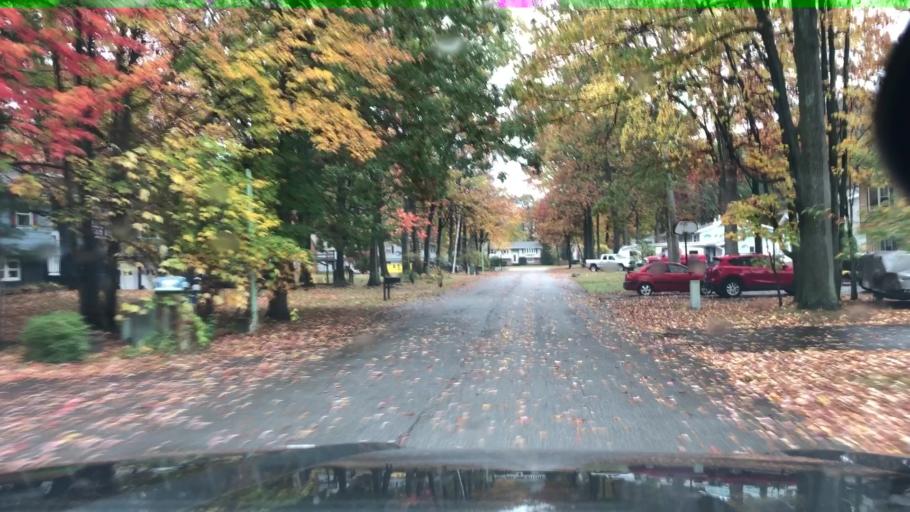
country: US
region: Vermont
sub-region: Chittenden County
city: Burlington
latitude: 44.5428
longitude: -73.2763
